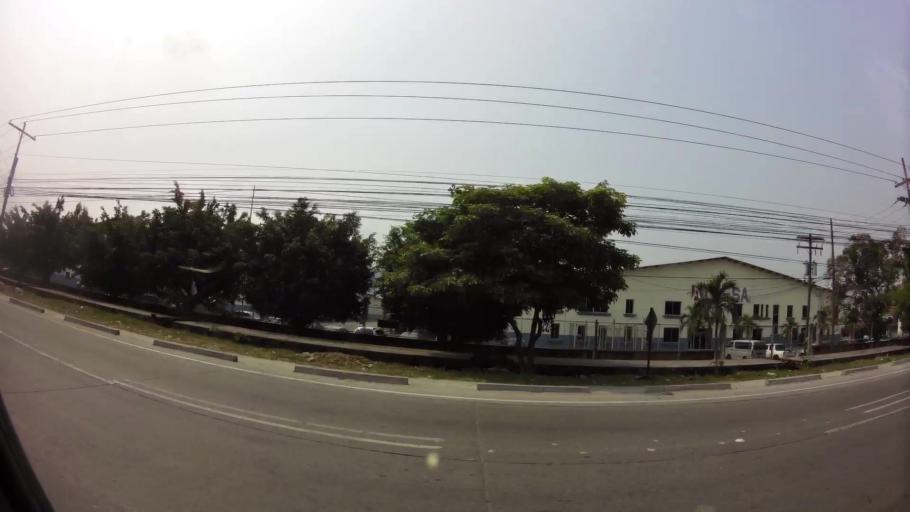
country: HN
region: Cortes
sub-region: San Pedro Sula
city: Pena Blanca
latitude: 15.5521
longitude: -88.0006
